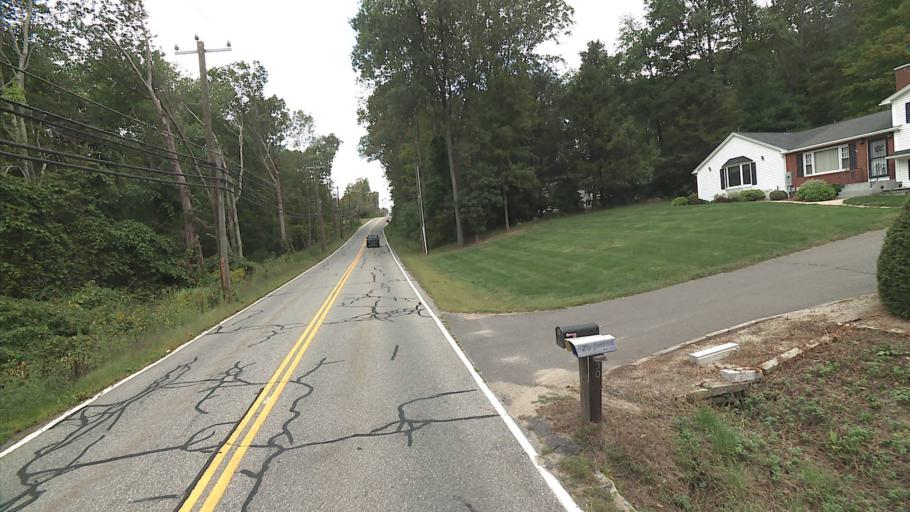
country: US
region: Connecticut
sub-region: Tolland County
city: Storrs
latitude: 41.8301
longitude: -72.2678
